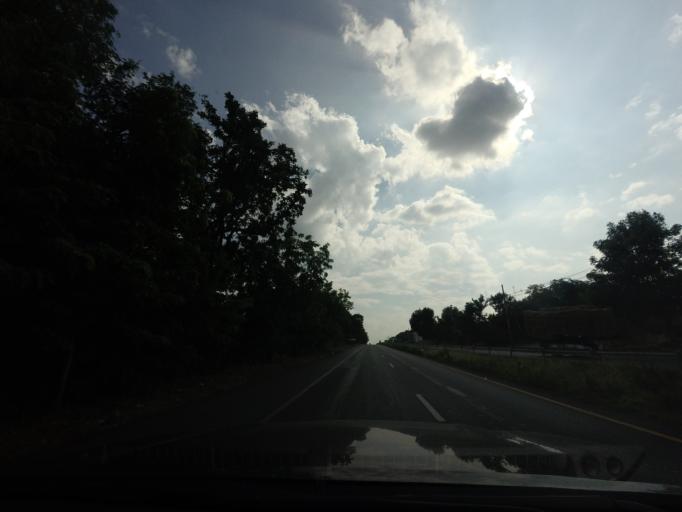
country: TH
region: Lop Buri
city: Chai Badan
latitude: 15.1585
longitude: 101.0578
